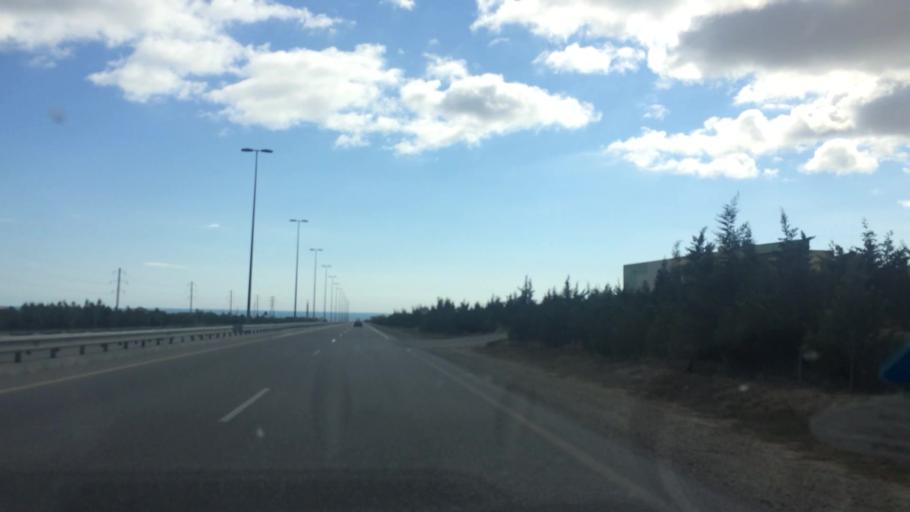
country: AZ
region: Baki
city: Zyrya
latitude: 40.4042
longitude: 50.3040
